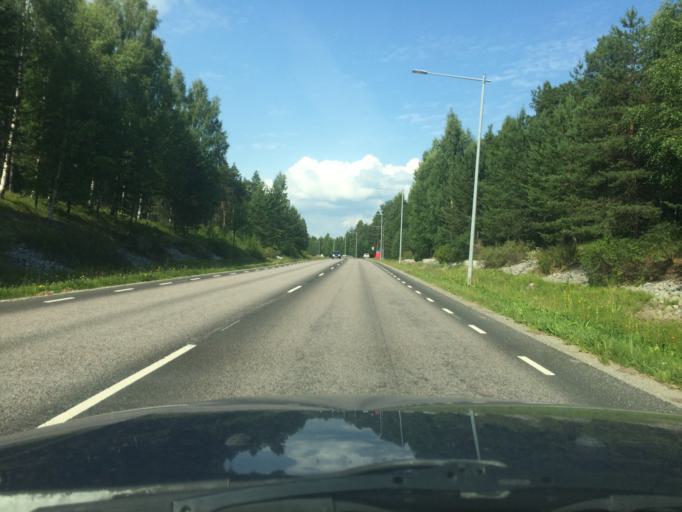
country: SE
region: Norrbotten
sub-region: Pitea Kommun
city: Pitea
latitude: 65.3269
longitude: 21.4757
